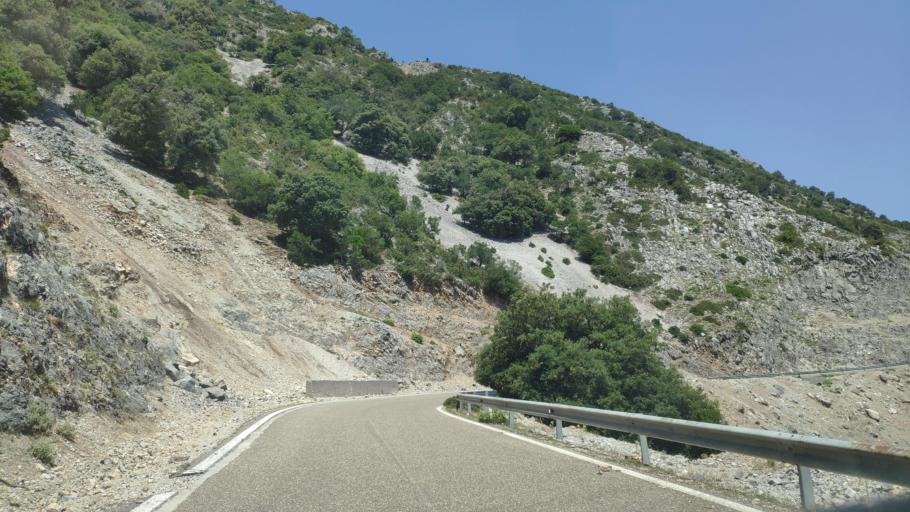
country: GR
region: West Greece
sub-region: Nomos Aitolias kai Akarnanias
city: Krikellos
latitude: 39.0181
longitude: 21.3691
